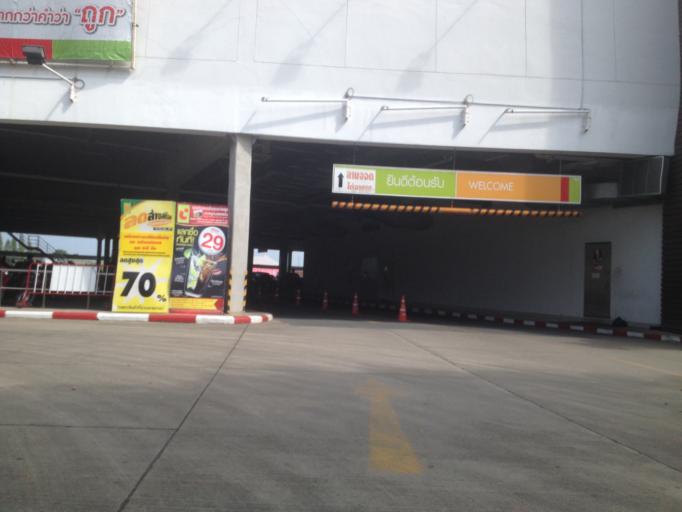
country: TH
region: Chiang Mai
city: Hang Dong
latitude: 18.6683
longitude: 98.9142
